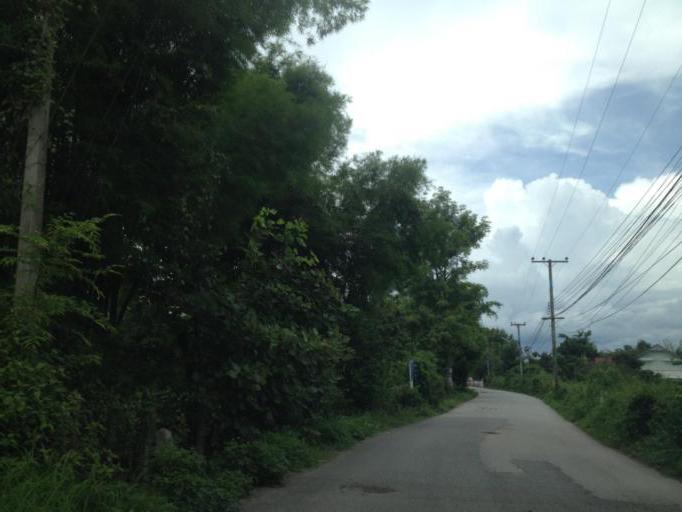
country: TH
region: Chiang Mai
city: Hang Dong
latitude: 18.6863
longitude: 98.8935
